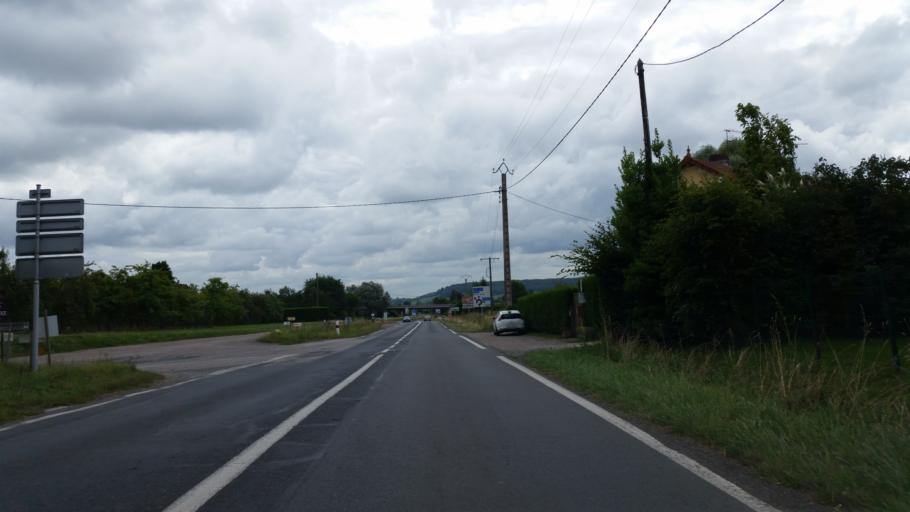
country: FR
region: Lower Normandy
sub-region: Departement du Calvados
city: Saint-Gatien-des-Bois
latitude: 49.3030
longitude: 0.1855
